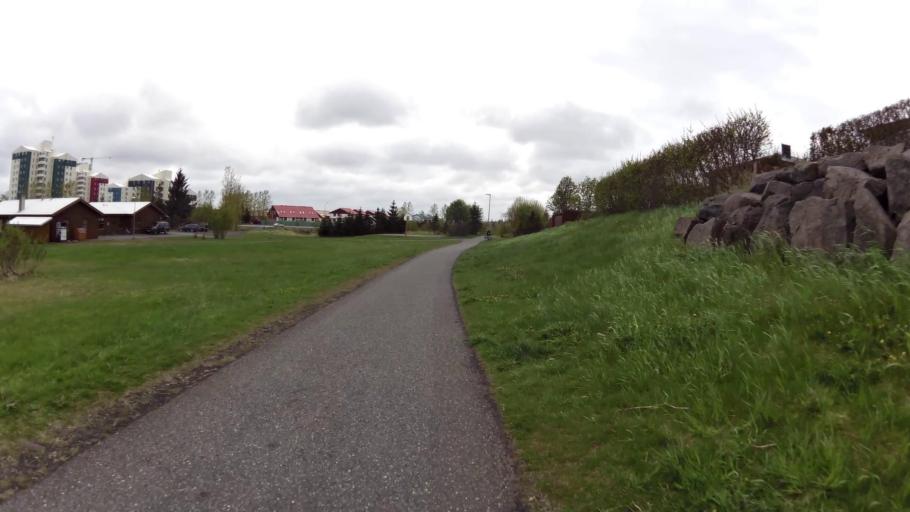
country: IS
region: Capital Region
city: Reykjavik
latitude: 64.1064
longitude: -21.8771
